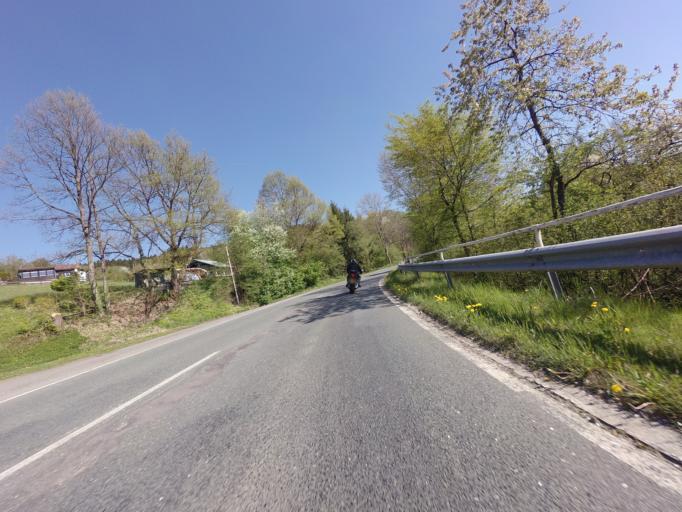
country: DE
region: North Rhine-Westphalia
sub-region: Regierungsbezirk Arnsberg
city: Olpe
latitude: 51.0949
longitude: 7.8292
